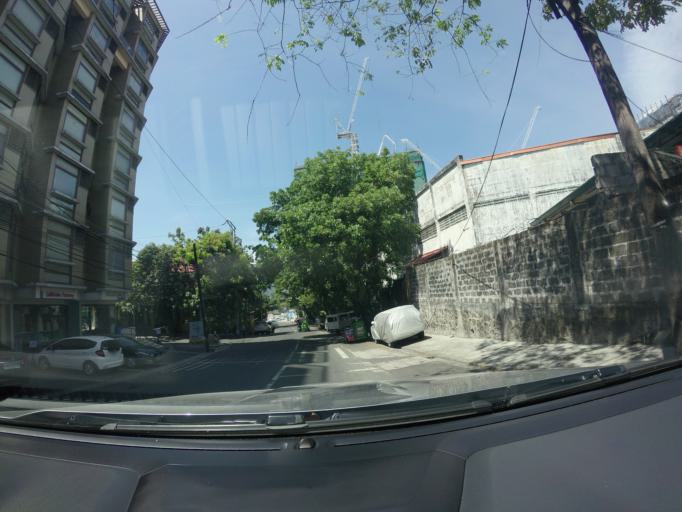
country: PH
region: Metro Manila
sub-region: Pasig
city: Pasig City
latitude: 14.5701
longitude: 121.0560
